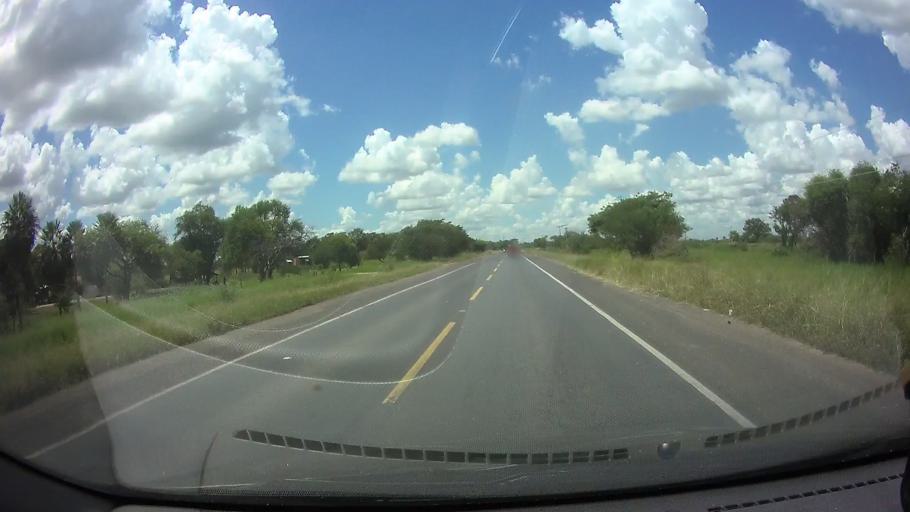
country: PY
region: Presidente Hayes
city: Nanawa
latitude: -25.1954
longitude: -57.6330
